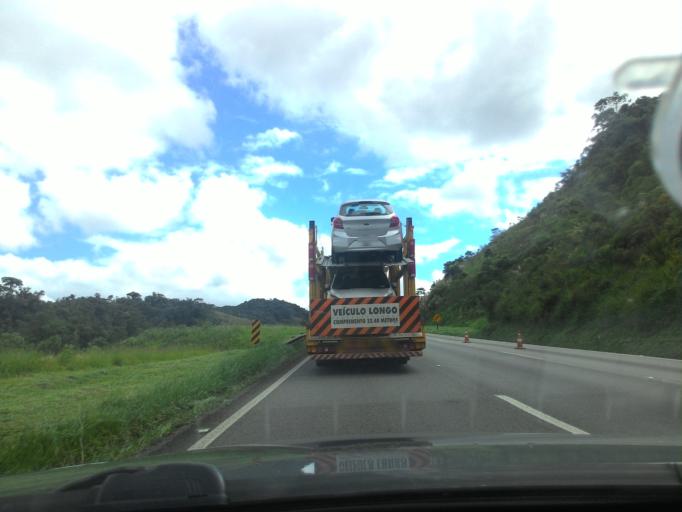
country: BR
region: Sao Paulo
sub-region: Cajati
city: Cajati
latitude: -24.8978
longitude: -48.2463
